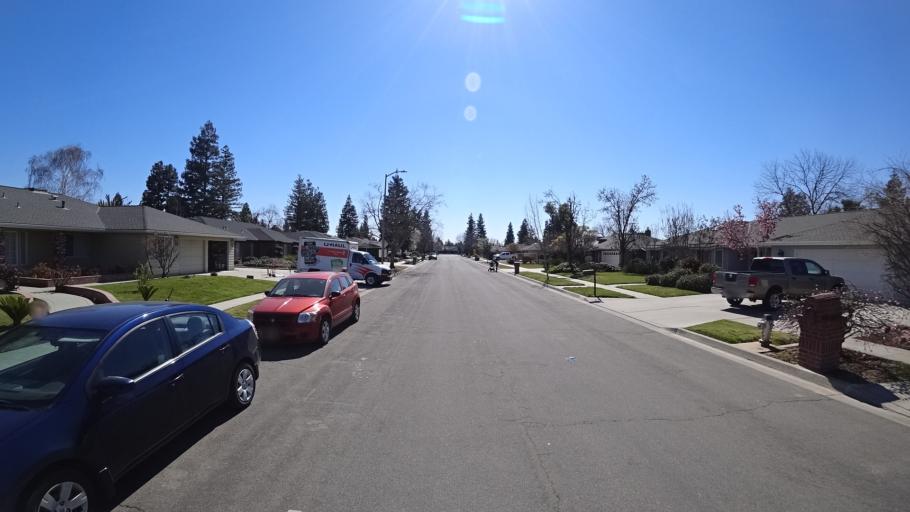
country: US
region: California
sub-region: Fresno County
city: Clovis
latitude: 36.8469
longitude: -119.7509
